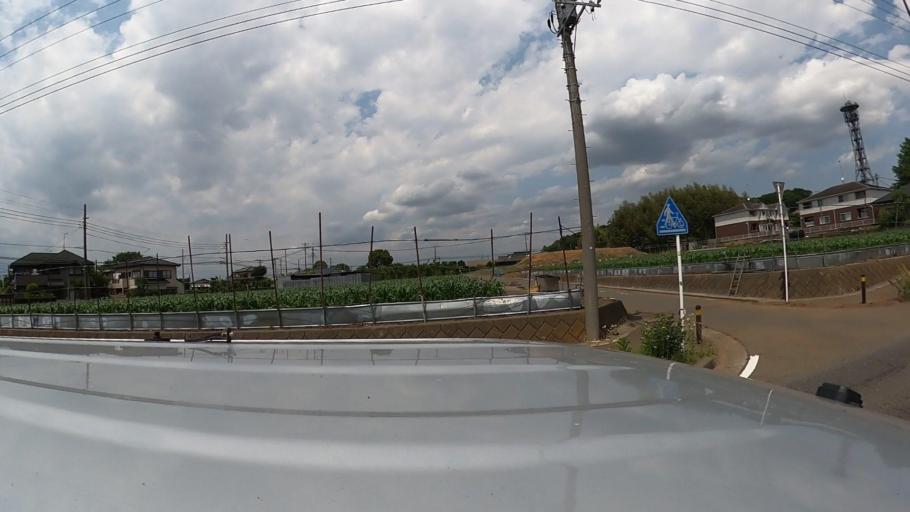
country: JP
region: Kanagawa
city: Chigasaki
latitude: 35.3933
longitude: 139.4173
